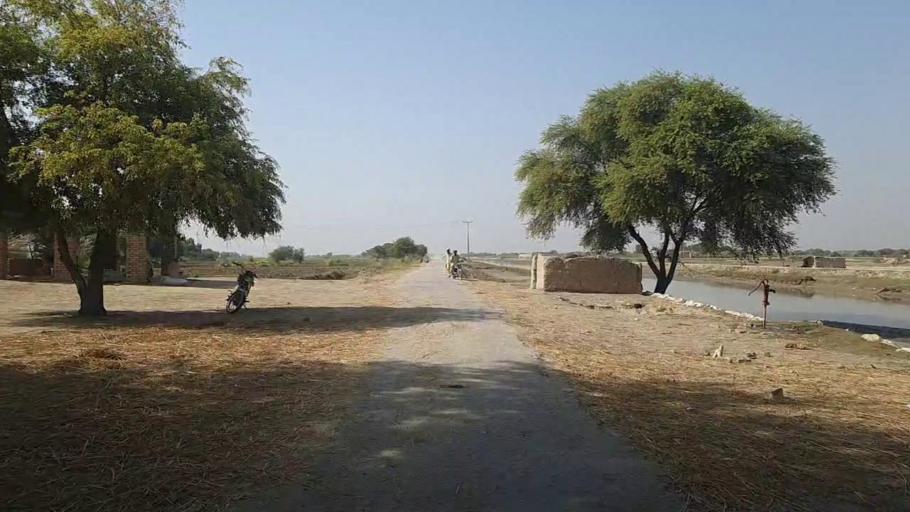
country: PK
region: Sindh
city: Kandhkot
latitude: 28.4132
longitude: 69.2400
